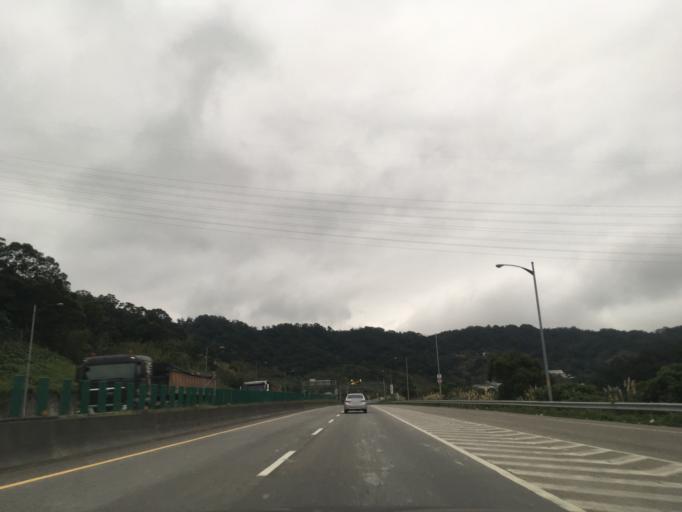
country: TW
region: Taipei
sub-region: Taipei
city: Banqiao
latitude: 25.1099
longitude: 121.4261
